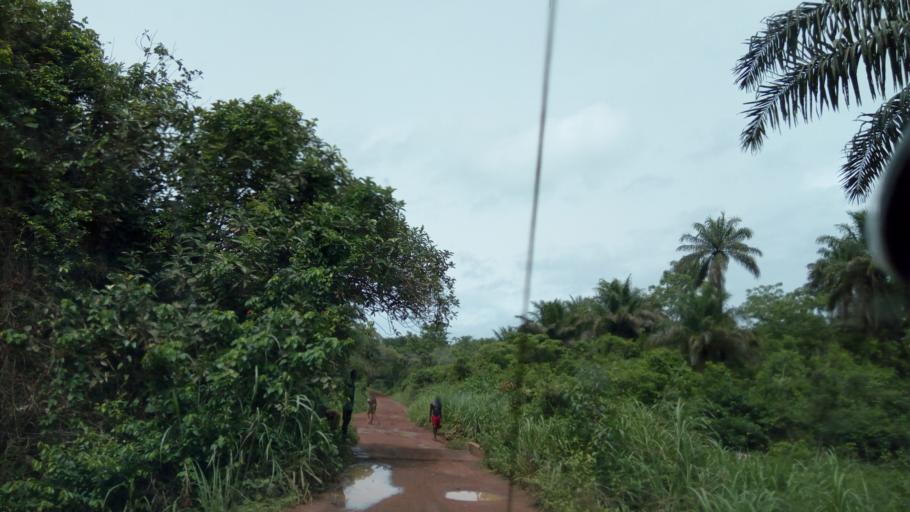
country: SL
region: Northern Province
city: Kambia
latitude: 9.1036
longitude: -12.9826
